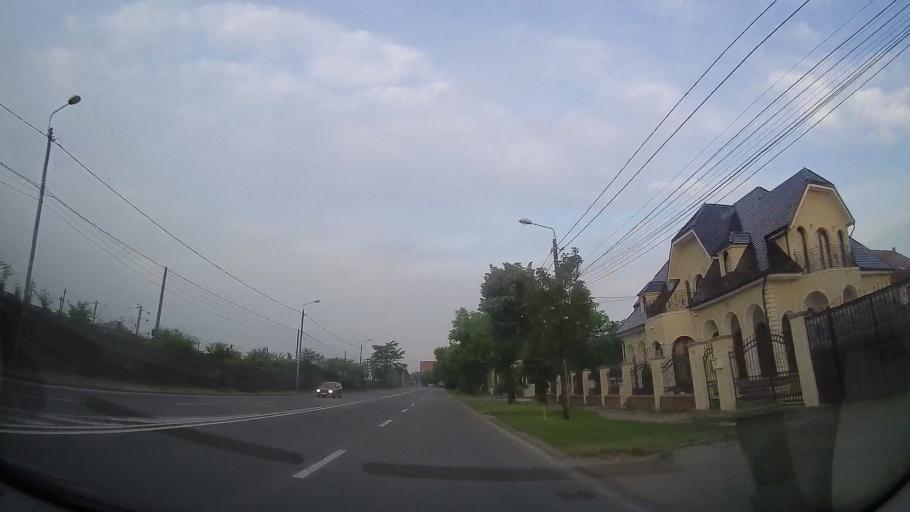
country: RO
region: Timis
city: Timisoara
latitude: 45.7694
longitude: 21.2477
